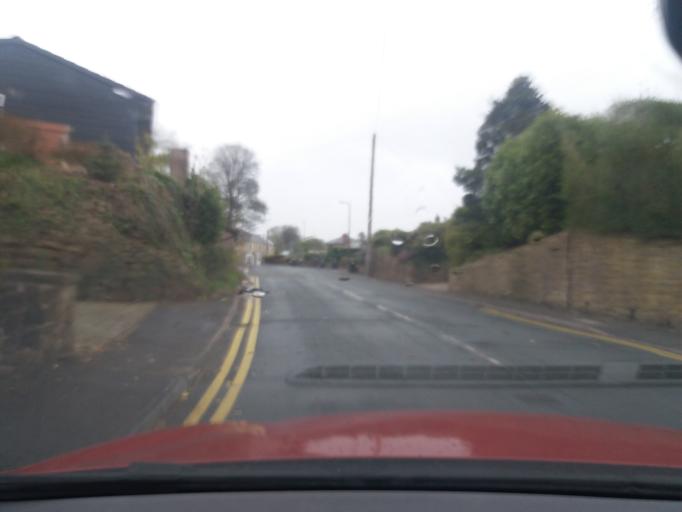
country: GB
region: England
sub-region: Lancashire
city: Clayton-le-Woods
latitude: 53.6868
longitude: -2.6352
